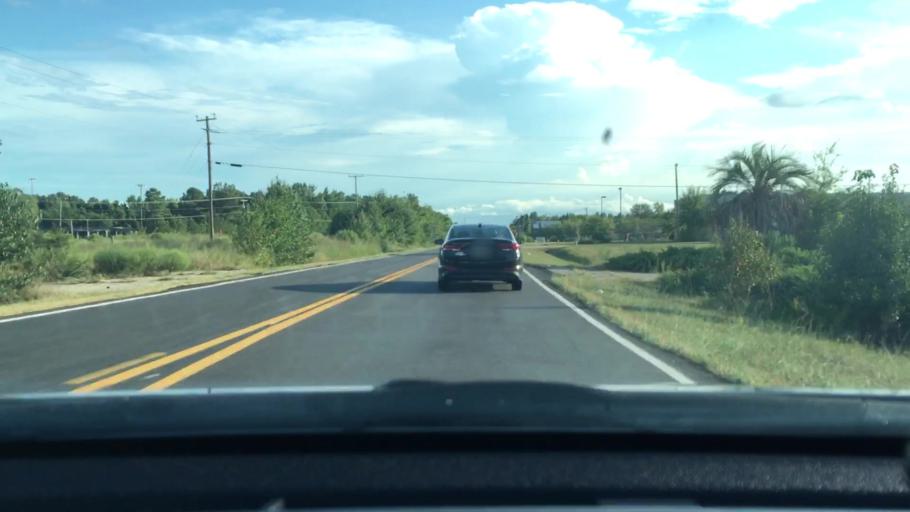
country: US
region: South Carolina
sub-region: Sumter County
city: South Sumter
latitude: 33.8848
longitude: -80.3504
